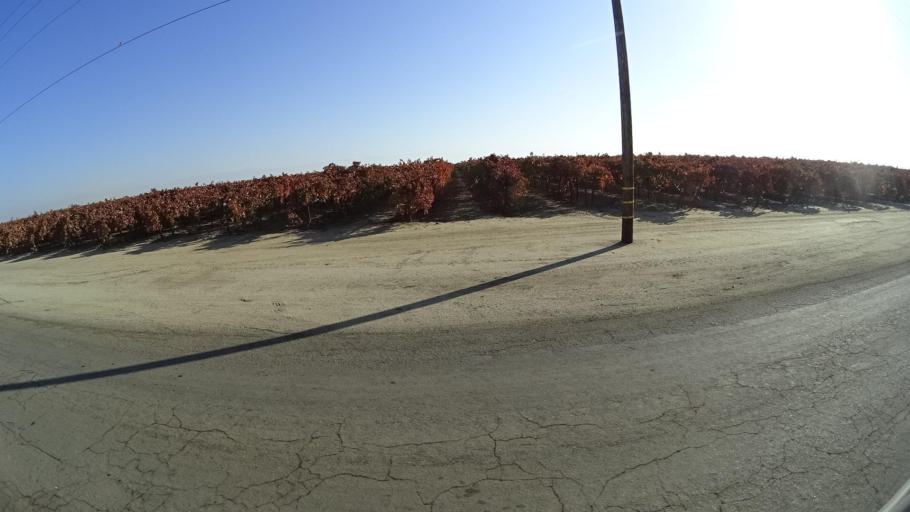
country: US
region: California
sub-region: Tulare County
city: Richgrove
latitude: 35.7572
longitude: -119.1696
